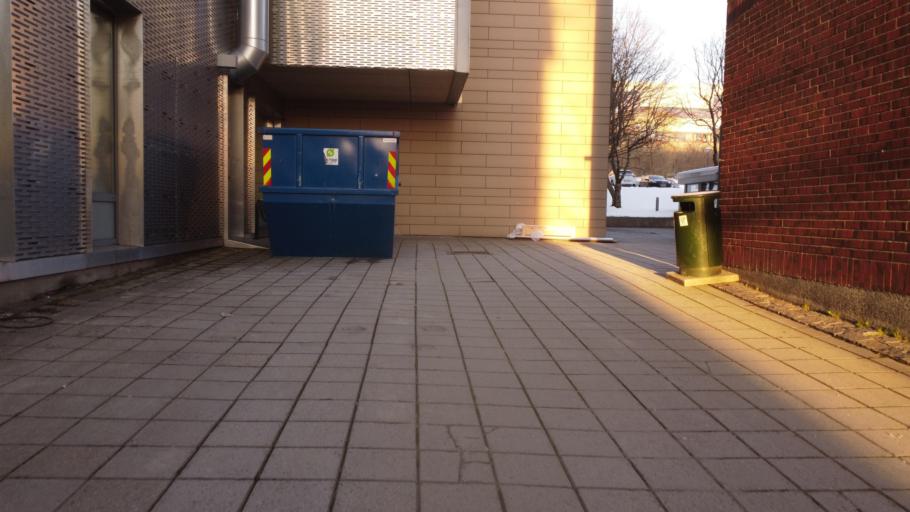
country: NO
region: Nordland
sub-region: Rana
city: Mo i Rana
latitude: 66.3112
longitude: 14.1376
